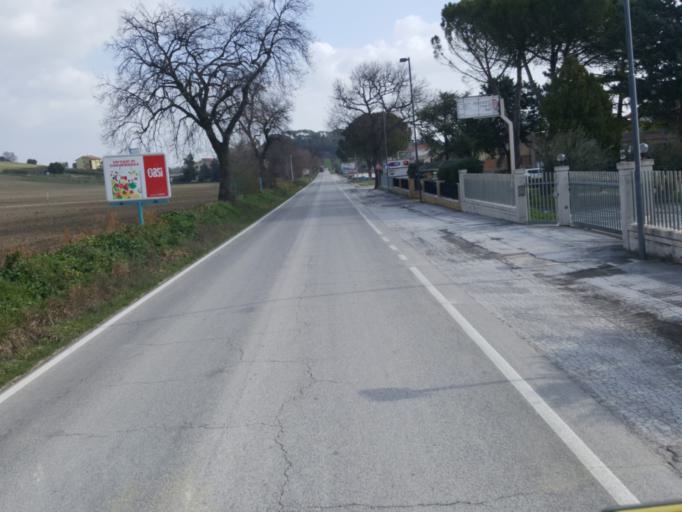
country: IT
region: The Marches
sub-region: Provincia di Macerata
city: Passo di Treia
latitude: 43.2917
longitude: 13.3396
